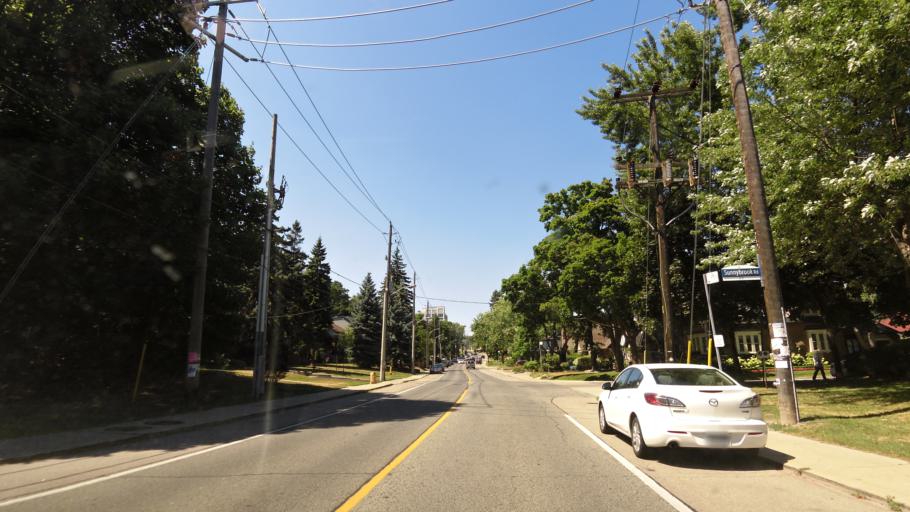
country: CA
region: Ontario
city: Etobicoke
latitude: 43.6451
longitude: -79.4826
